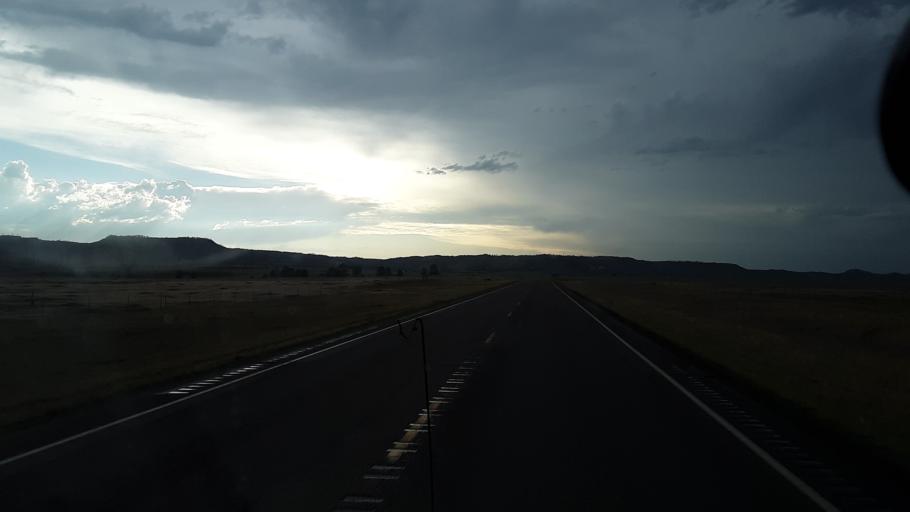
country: US
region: Montana
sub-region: Rosebud County
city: Lame Deer
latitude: 45.6105
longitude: -106.3527
